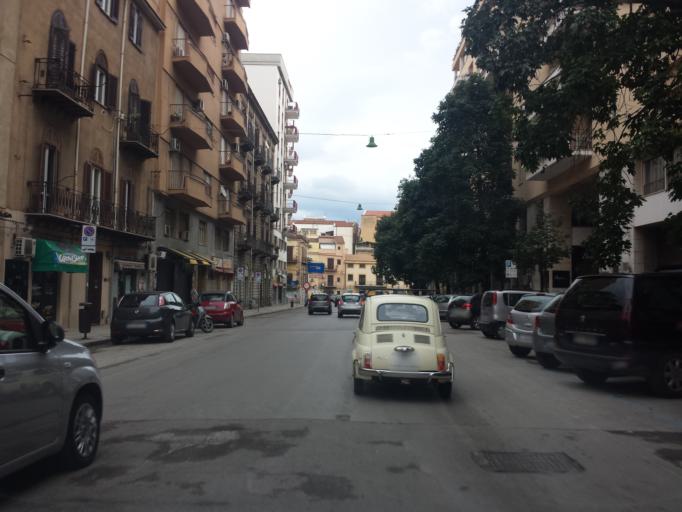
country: IT
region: Sicily
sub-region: Palermo
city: Palermo
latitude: 38.1200
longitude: 13.3515
